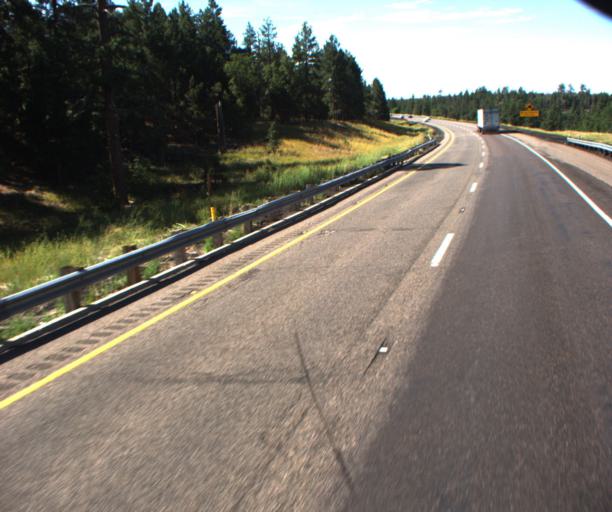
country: US
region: Arizona
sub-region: Yavapai County
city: Village of Oak Creek (Big Park)
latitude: 34.8212
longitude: -111.6135
